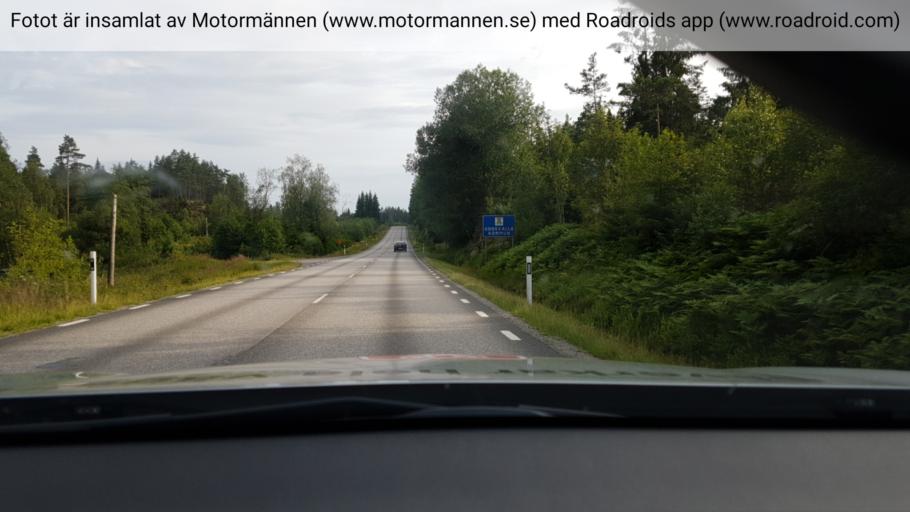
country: SE
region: Vaestra Goetaland
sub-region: Fargelanda Kommun
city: Faergelanda
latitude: 58.4463
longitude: 12.0236
